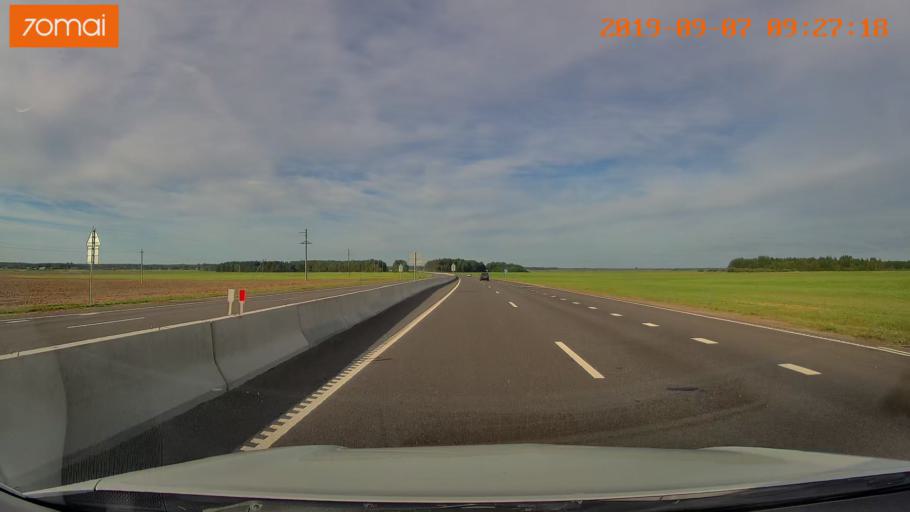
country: BY
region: Grodnenskaya
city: Lyubcha
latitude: 53.9131
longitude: 26.0809
